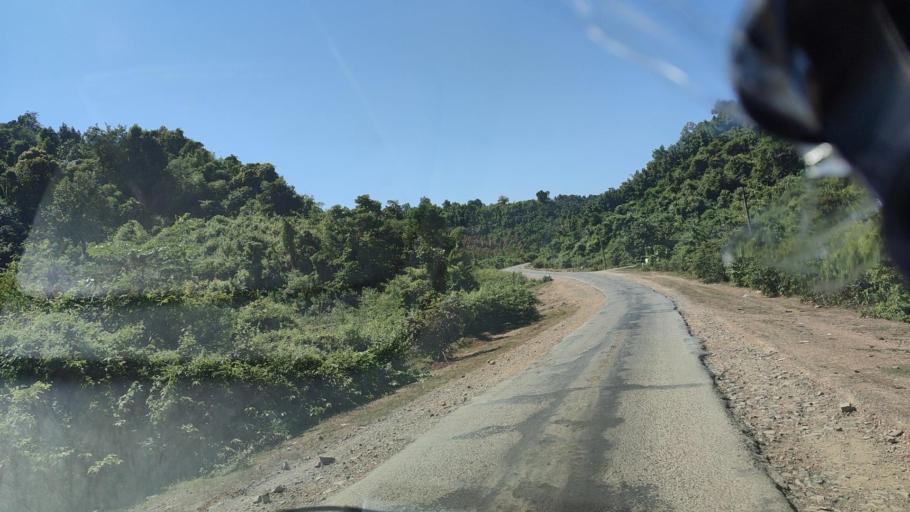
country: MM
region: Rakhine
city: Sittwe
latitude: 20.1328
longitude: 93.4742
